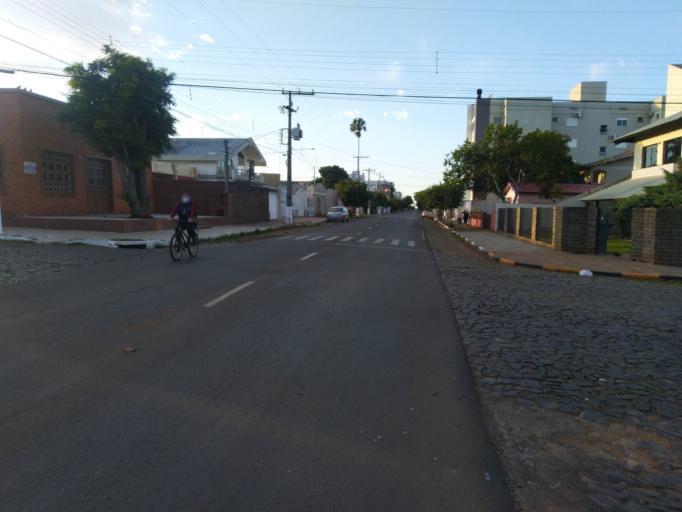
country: BR
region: Rio Grande do Sul
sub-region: Sao Borja
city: Sao Borja
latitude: -28.6569
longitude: -56.0097
